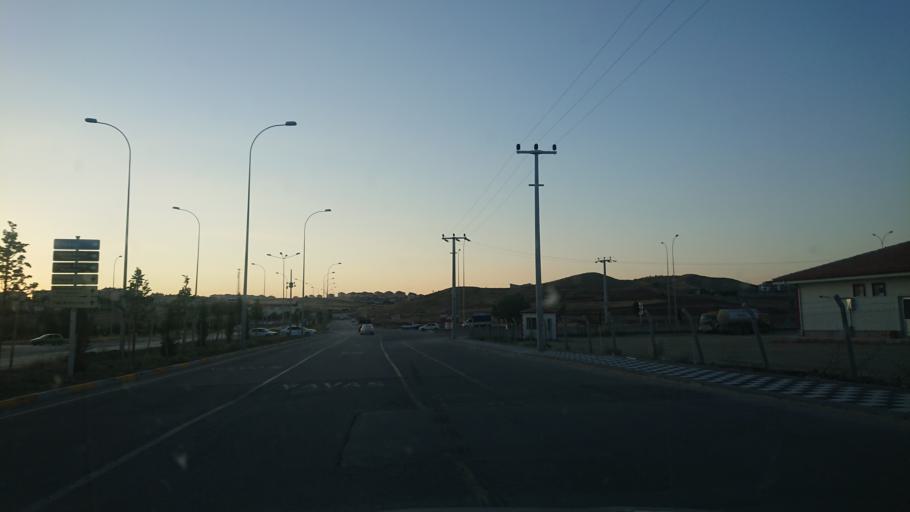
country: TR
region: Aksaray
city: Aksaray
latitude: 38.4097
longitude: 34.0118
